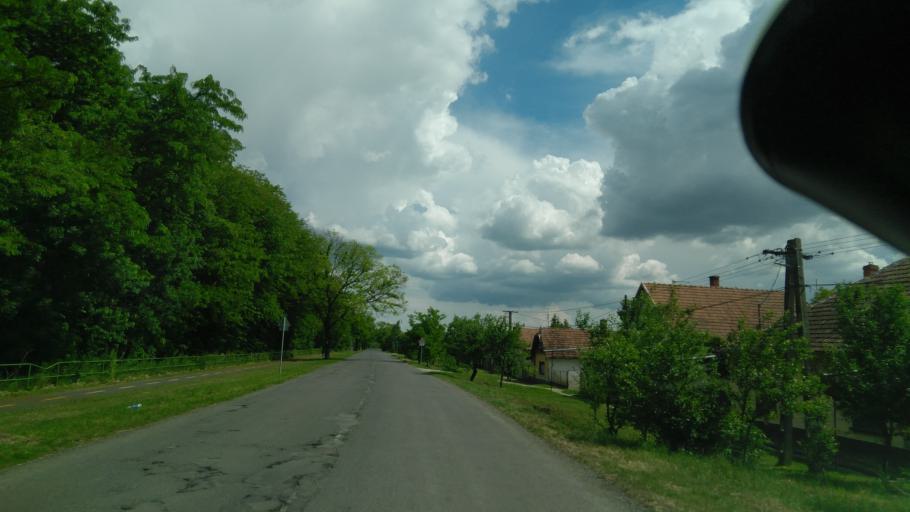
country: HU
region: Bekes
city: Korosladany
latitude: 46.9717
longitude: 21.0632
